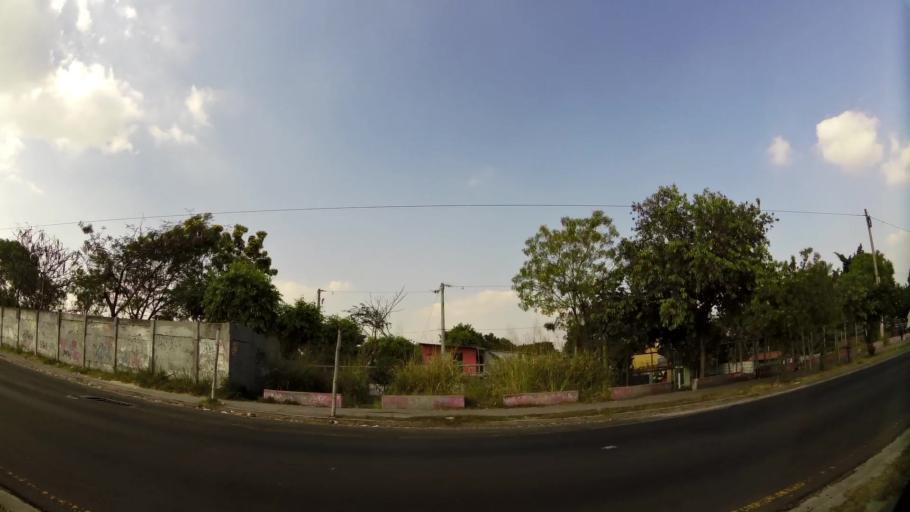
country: SV
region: San Salvador
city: Soyapango
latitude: 13.7169
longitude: -89.1383
